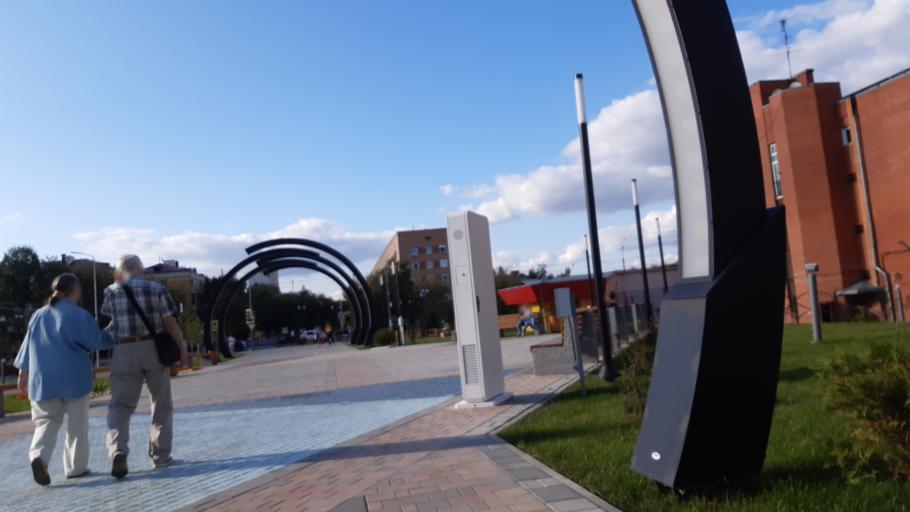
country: RU
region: Moskovskaya
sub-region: Podol'skiy Rayon
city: Podol'sk
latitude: 55.4265
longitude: 37.5342
